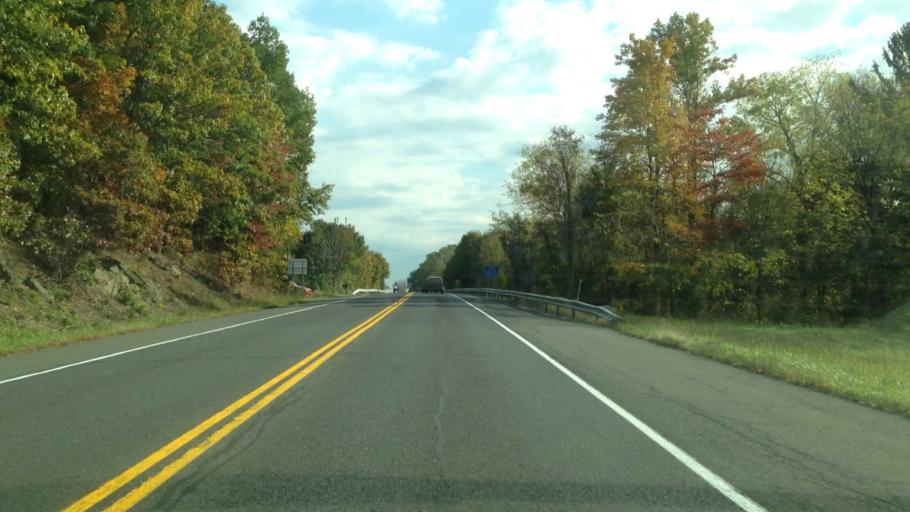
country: US
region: New York
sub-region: Ulster County
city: Highland
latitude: 41.7395
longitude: -74.0076
